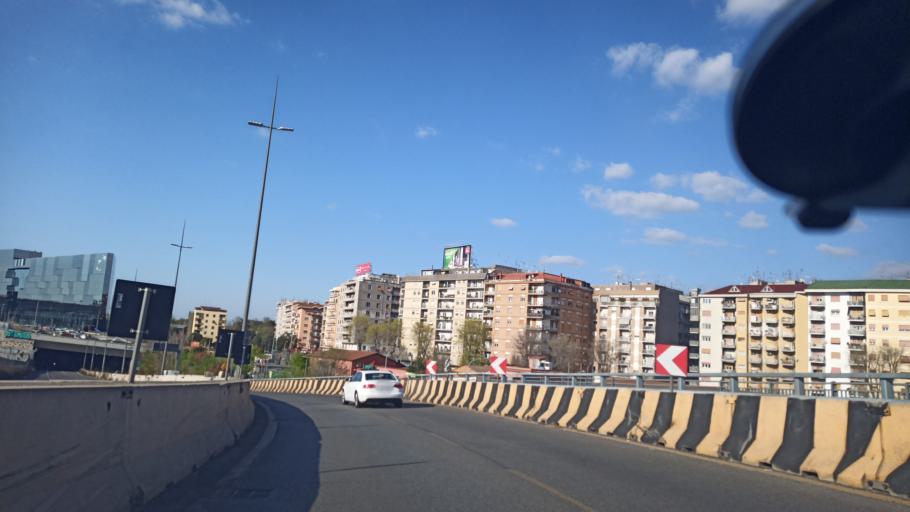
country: IT
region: Latium
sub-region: Citta metropolitana di Roma Capitale
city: Rome
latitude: 41.9061
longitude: 12.5342
